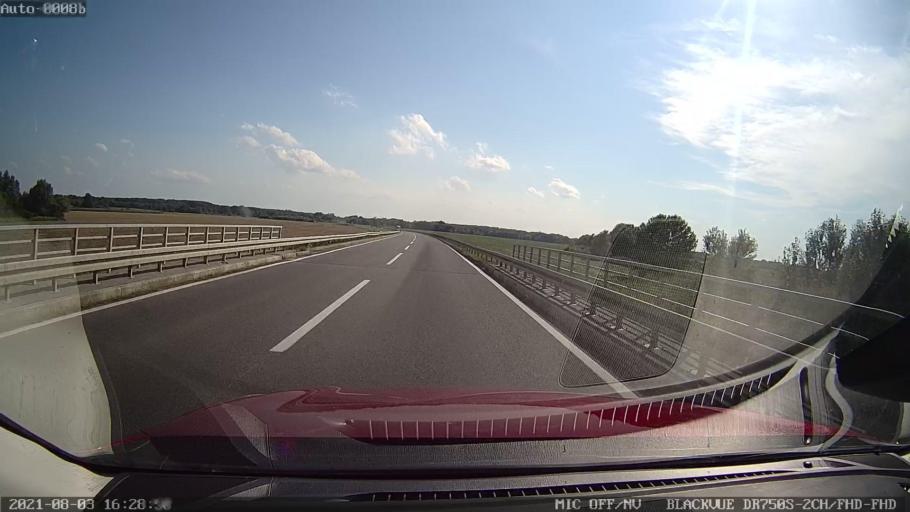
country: HR
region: Osjecko-Baranjska
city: Darda
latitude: 45.6049
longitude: 18.6611
